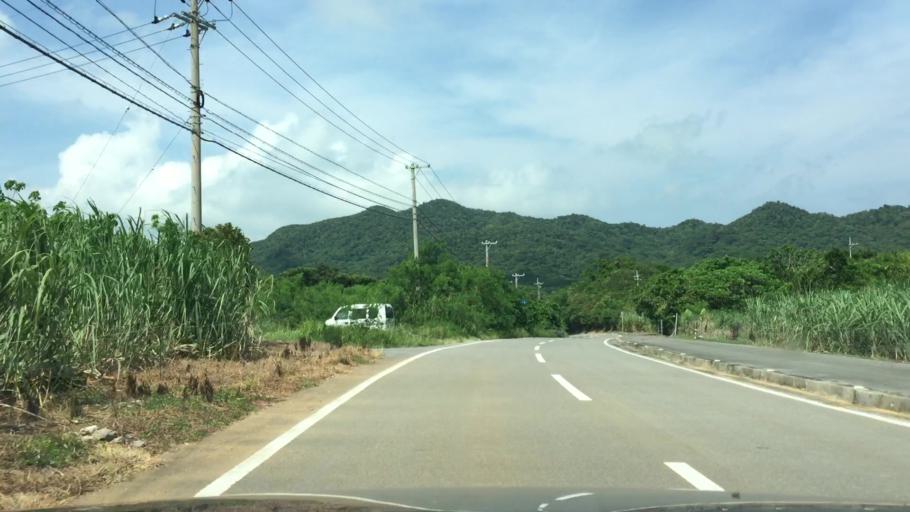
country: JP
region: Okinawa
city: Ishigaki
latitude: 24.5005
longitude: 124.2512
